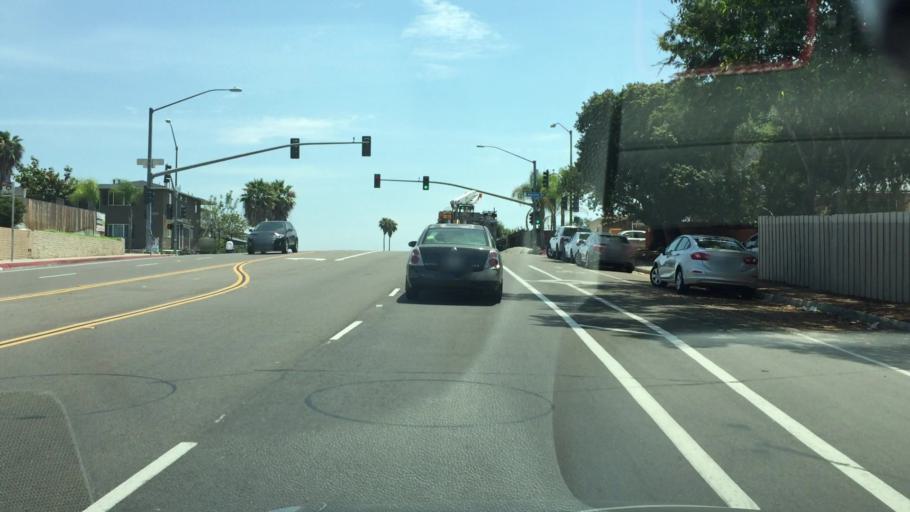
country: US
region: California
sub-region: San Diego County
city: Lemon Grove
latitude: 32.7584
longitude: -117.0664
